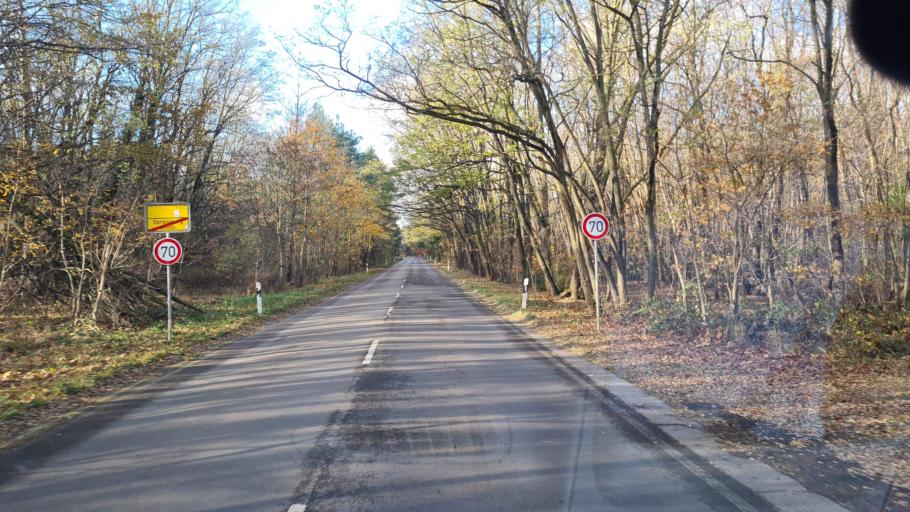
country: DE
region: Brandenburg
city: Spremberg
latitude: 51.5793
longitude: 14.3485
